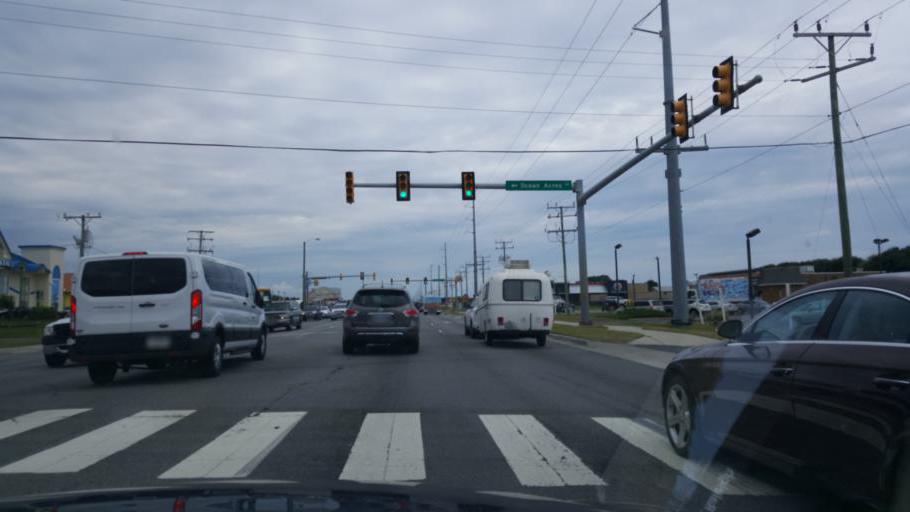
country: US
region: North Carolina
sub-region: Dare County
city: Kill Devil Hills
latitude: 35.9976
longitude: -75.6513
